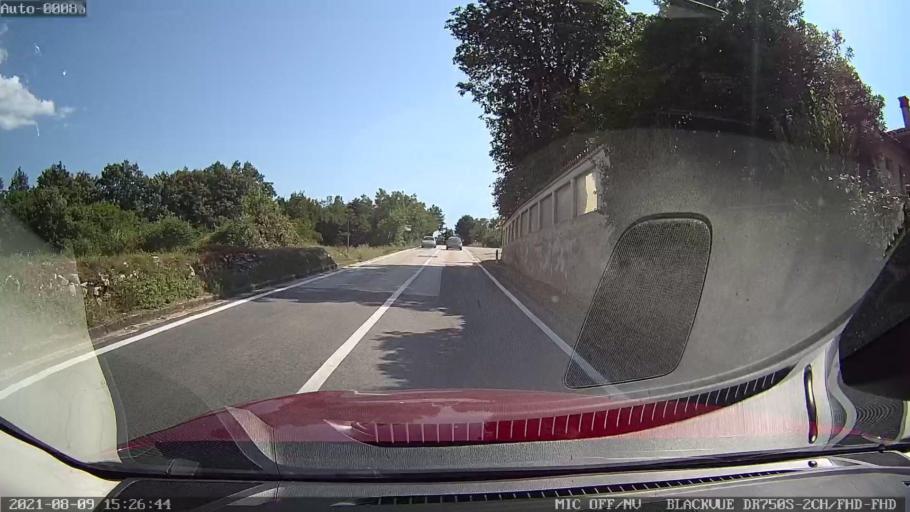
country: HR
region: Istarska
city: Pazin
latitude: 45.1594
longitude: 13.9072
